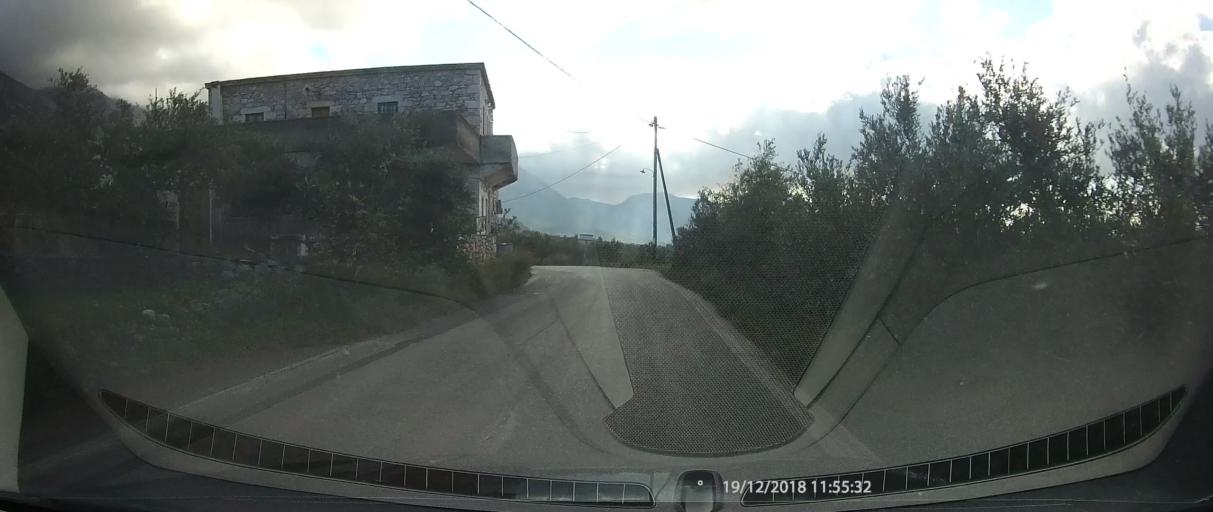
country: GR
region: Peloponnese
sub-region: Nomos Lakonias
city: Gytheio
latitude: 36.6074
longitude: 22.3945
